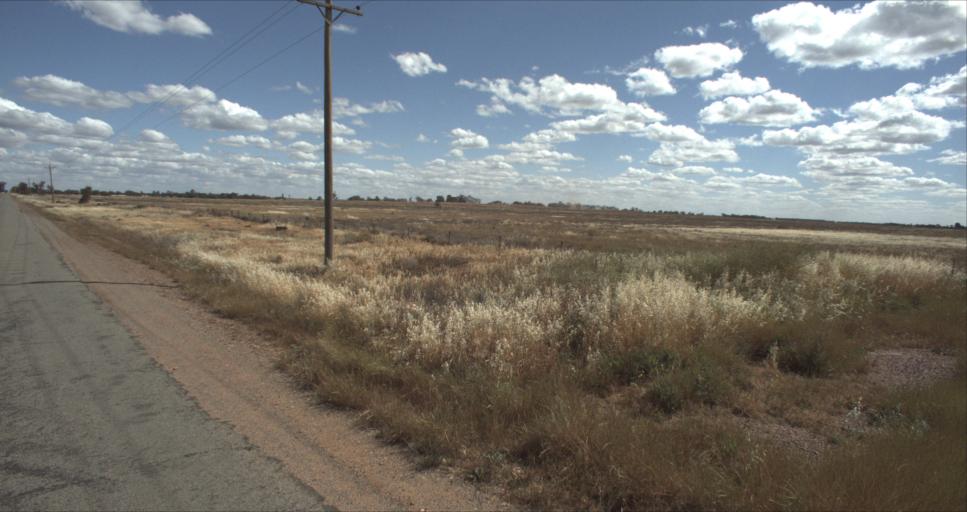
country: AU
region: New South Wales
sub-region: Leeton
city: Leeton
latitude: -34.4749
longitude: 146.2502
